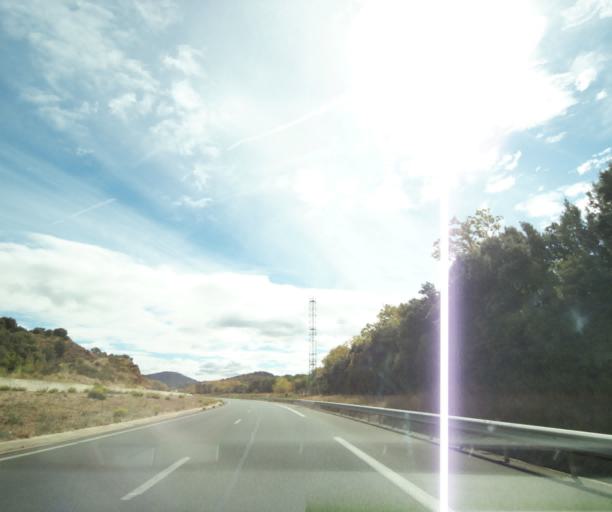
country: FR
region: Languedoc-Roussillon
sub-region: Departement de l'Herault
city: Lodeve
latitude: 43.7012
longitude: 3.3305
